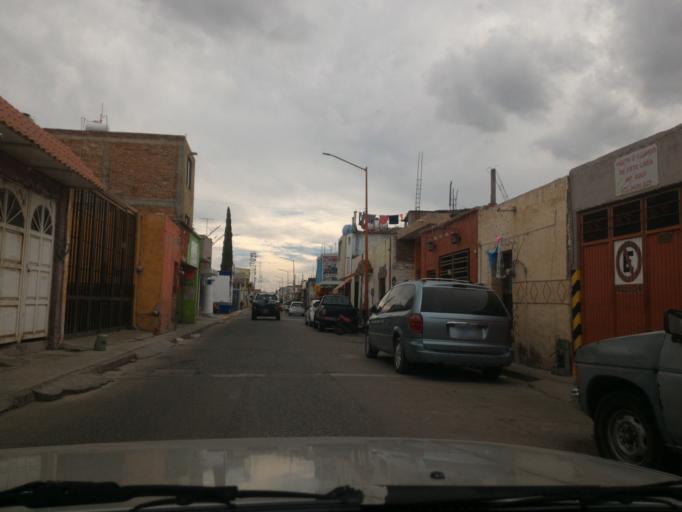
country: MX
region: Guanajuato
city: San Francisco del Rincon
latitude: 21.0233
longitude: -101.8604
